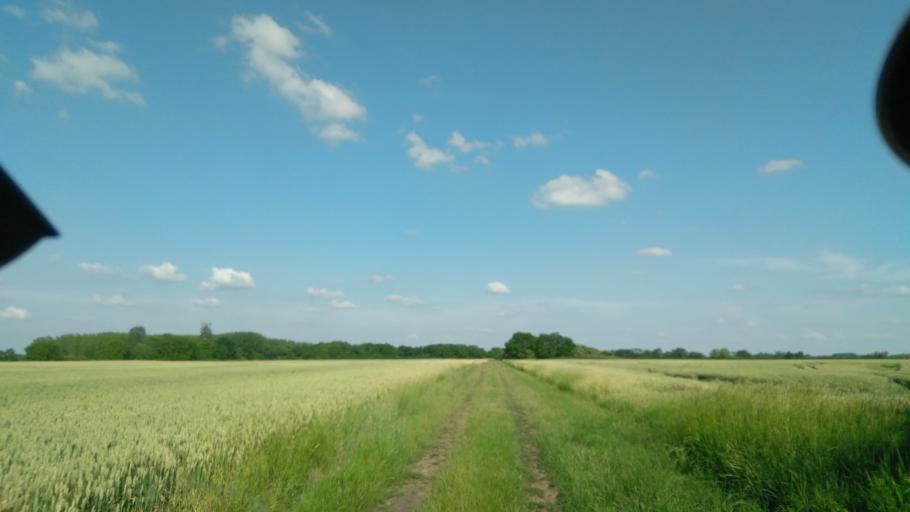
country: HU
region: Bekes
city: Doboz
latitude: 46.6991
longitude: 21.2261
